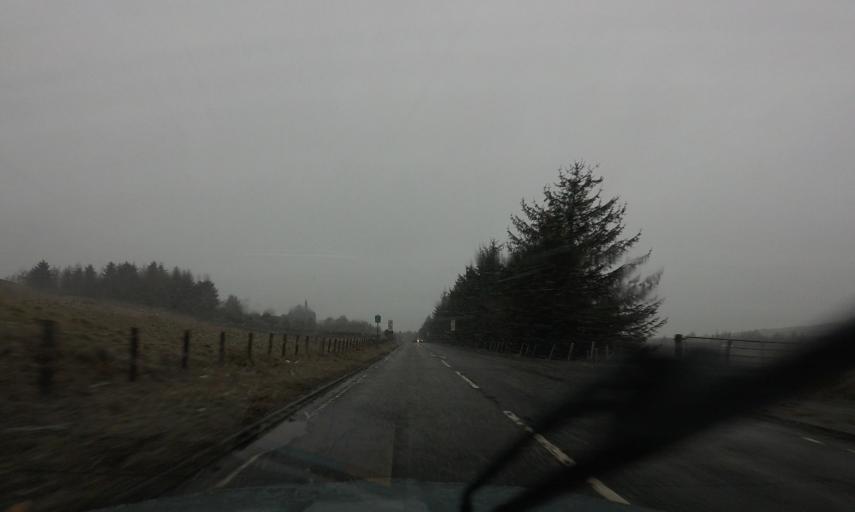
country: GB
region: Scotland
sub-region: North Lanarkshire
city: Shotts
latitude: 55.8469
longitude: -3.8442
